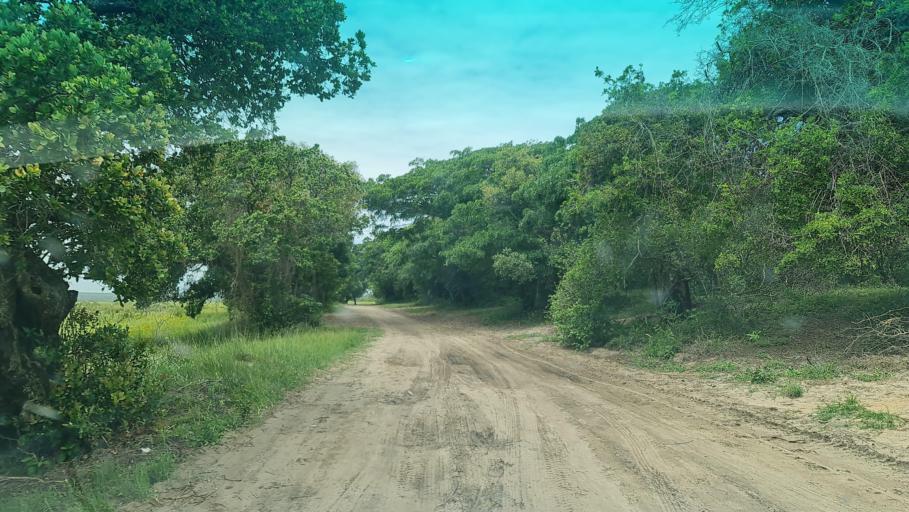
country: MZ
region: Maputo
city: Manhica
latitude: -25.5303
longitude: 32.8460
